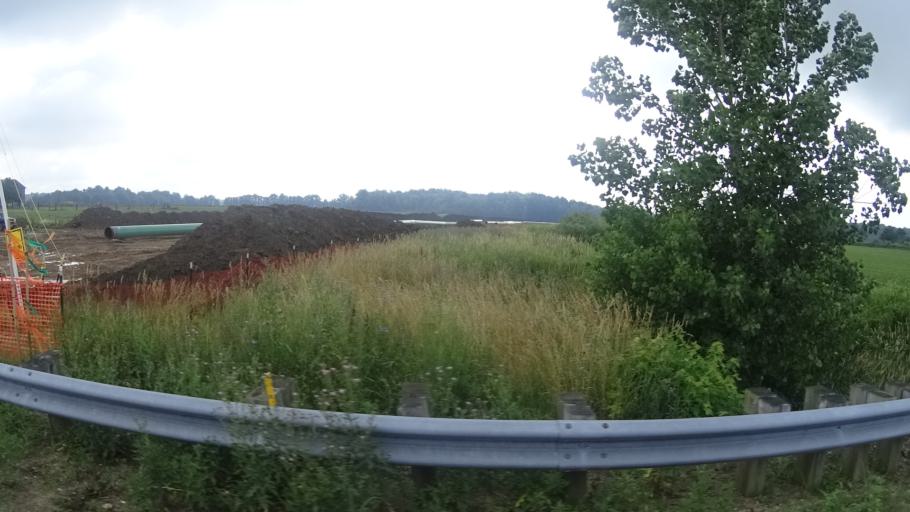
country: US
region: Ohio
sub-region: Huron County
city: Wakeman
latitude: 41.3018
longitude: -82.4429
